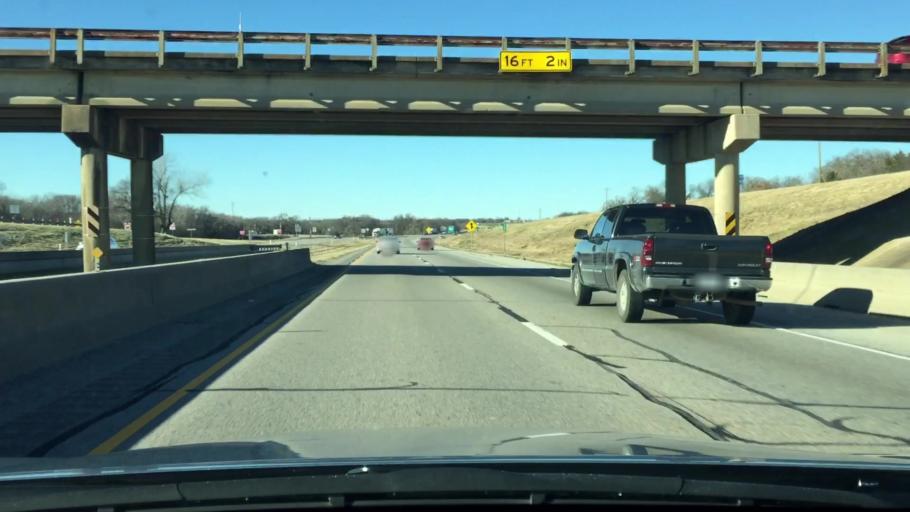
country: US
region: Texas
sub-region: Johnson County
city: Grandview
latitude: 32.2862
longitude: -97.1771
